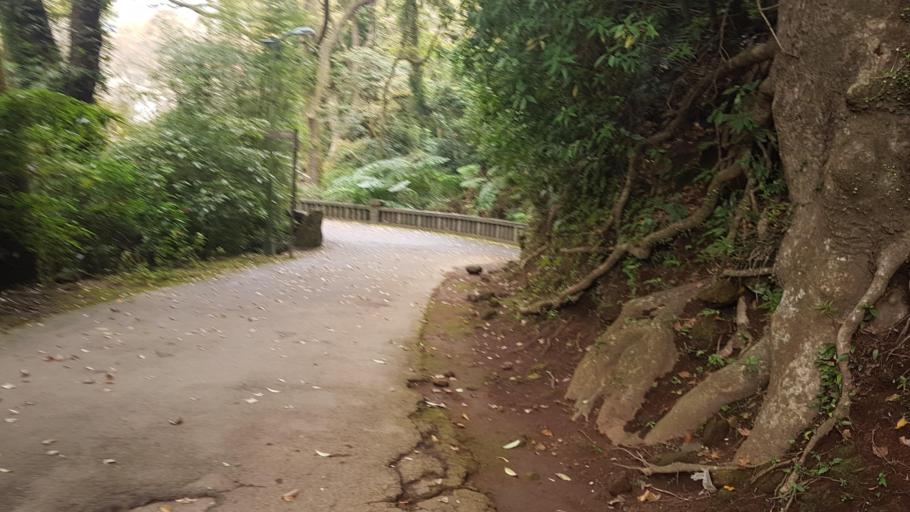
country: TW
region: Taipei
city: Taipei
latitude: 25.1575
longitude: 121.5408
